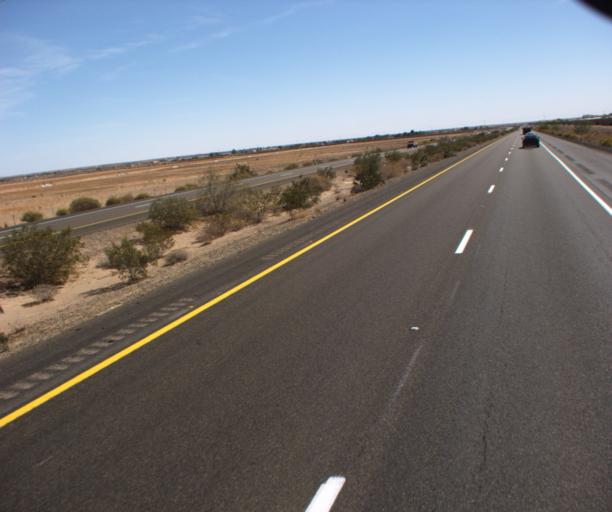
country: US
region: Arizona
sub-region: Yuma County
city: Fortuna Foothills
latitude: 32.6492
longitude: -114.5216
